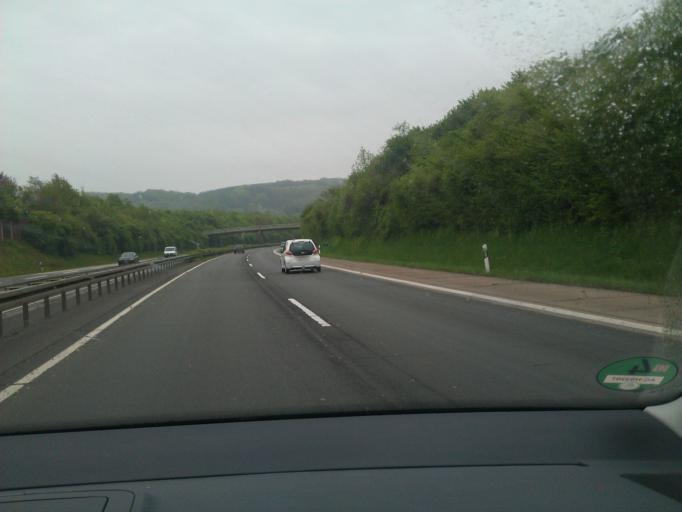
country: DE
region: North Rhine-Westphalia
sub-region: Regierungsbezirk Koln
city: Hennef
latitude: 50.7827
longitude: 7.2724
